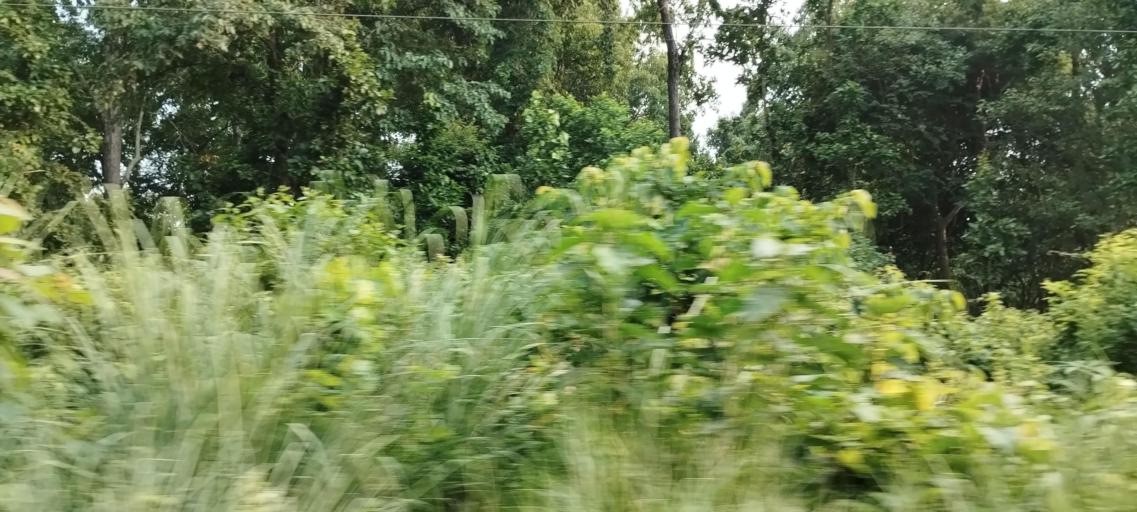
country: NP
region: Mid Western
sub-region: Bheri Zone
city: Bardiya
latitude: 28.4301
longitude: 81.3501
